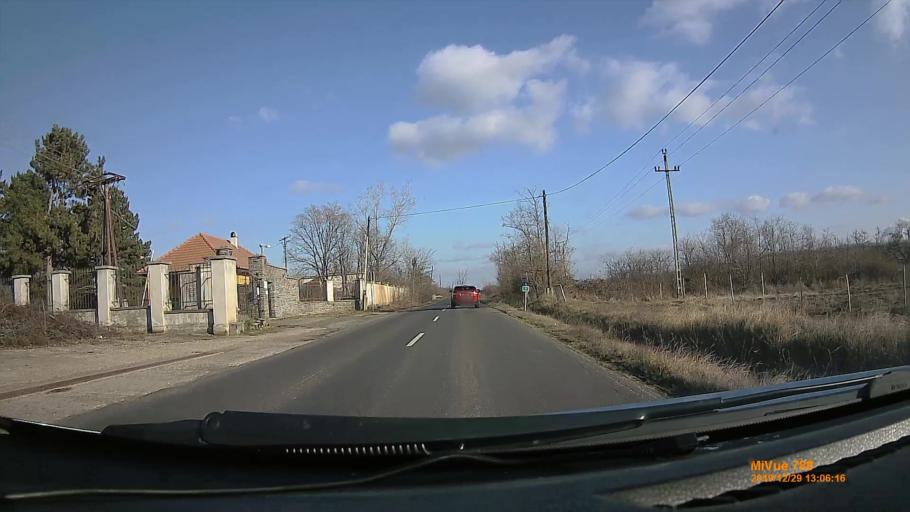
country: HU
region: Heves
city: Abasar
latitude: 47.8071
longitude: 20.0255
